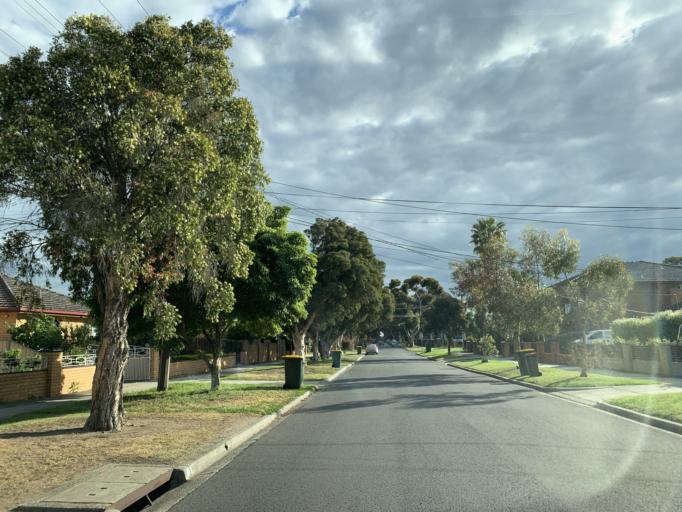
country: AU
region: Victoria
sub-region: Moonee Valley
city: Essendon West
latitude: -37.7541
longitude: 144.8575
